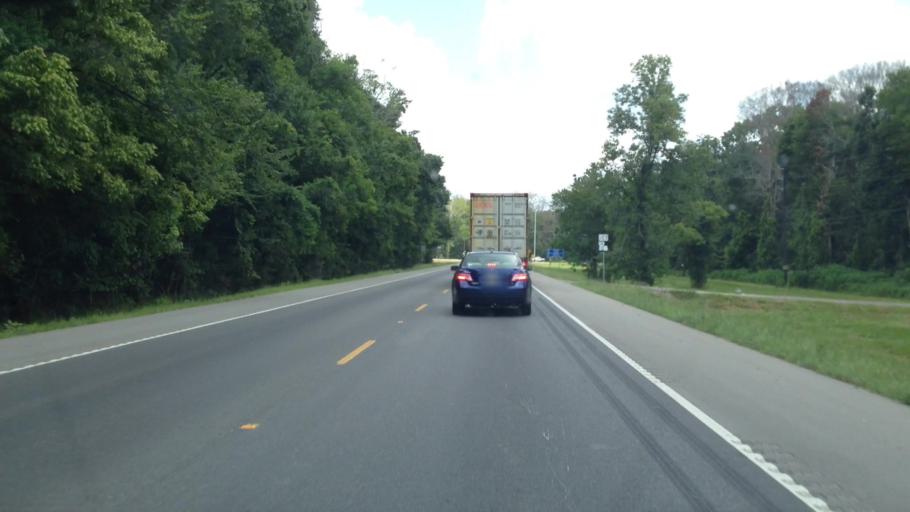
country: US
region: Louisiana
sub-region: Ascension Parish
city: Sorrento
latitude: 30.1637
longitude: -90.8798
